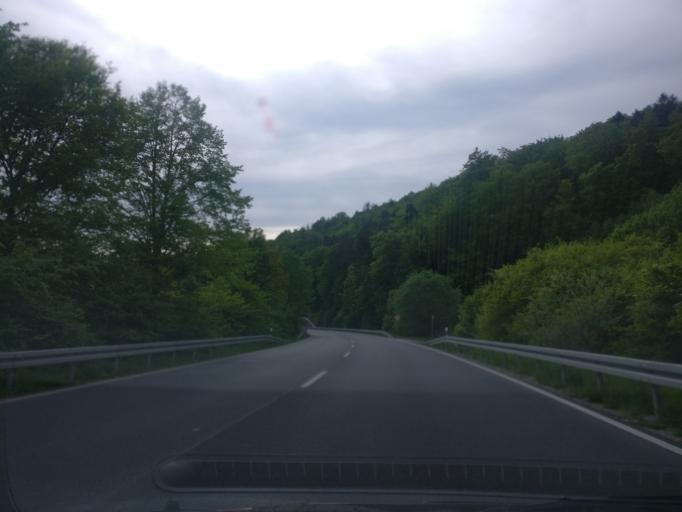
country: DE
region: Hesse
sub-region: Regierungsbezirk Kassel
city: Fuldatal
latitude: 51.3697
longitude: 9.5359
